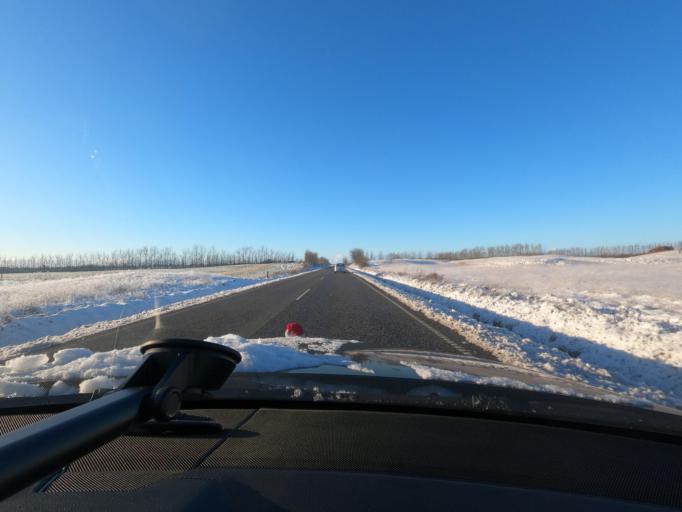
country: DK
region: South Denmark
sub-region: Tonder Kommune
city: Sherrebek
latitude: 55.1765
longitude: 8.8248
